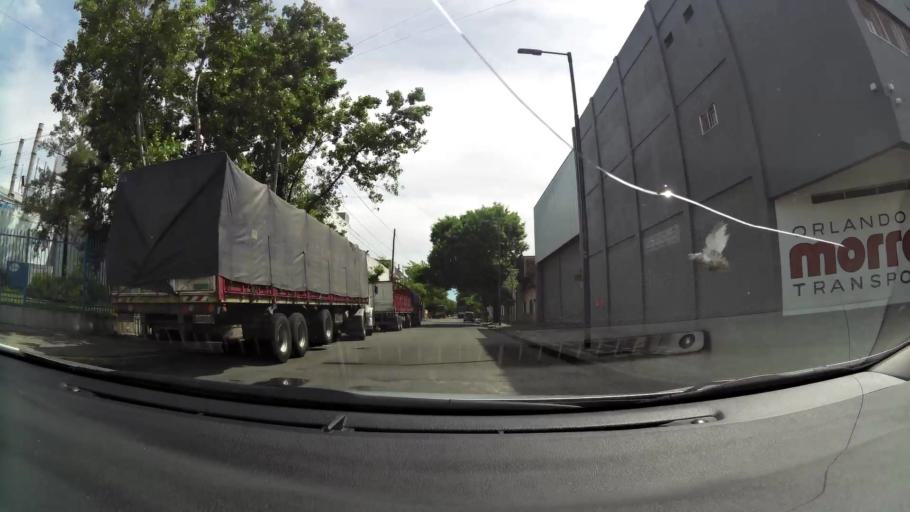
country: AR
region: Buenos Aires F.D.
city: Villa Lugano
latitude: -34.6621
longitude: -58.4272
